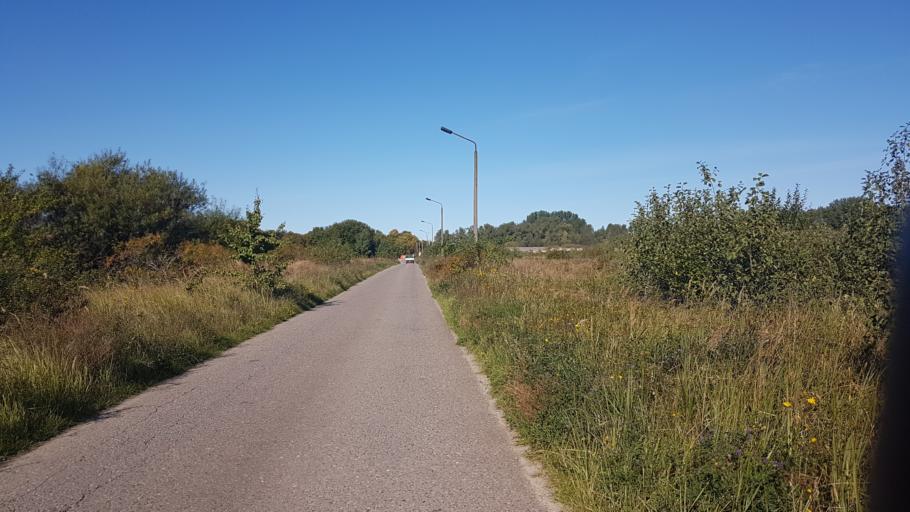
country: DE
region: Mecklenburg-Vorpommern
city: Sagard
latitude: 54.4998
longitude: 13.5403
